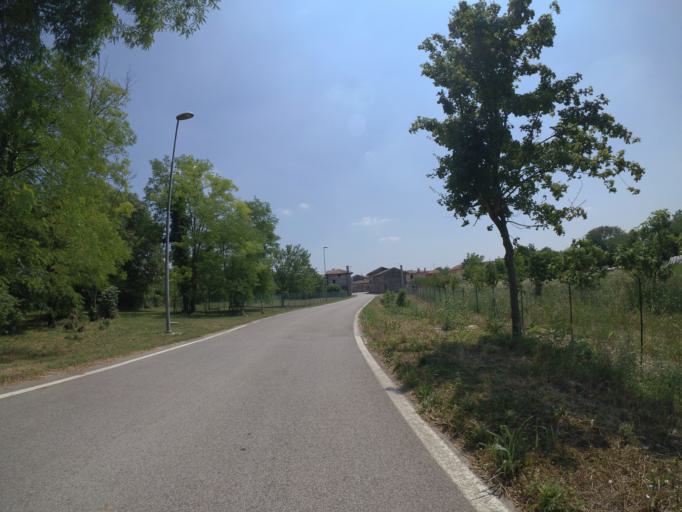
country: IT
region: Friuli Venezia Giulia
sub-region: Provincia di Udine
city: Codroipo
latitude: 45.9662
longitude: 13.0023
